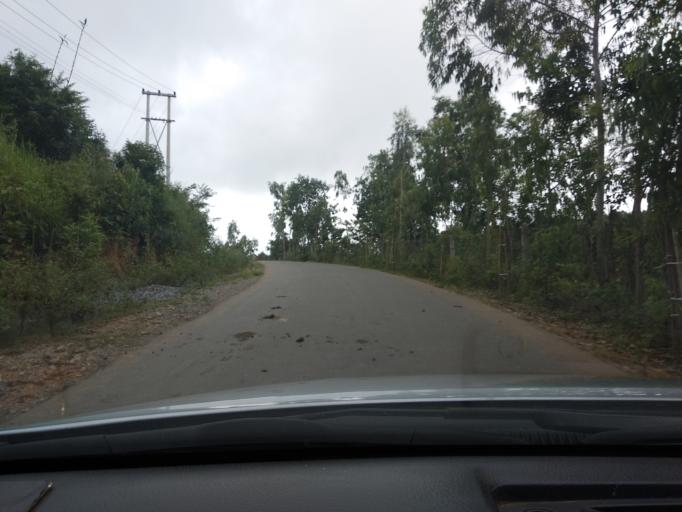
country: MM
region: Mandalay
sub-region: Pyin Oo Lwin District
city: Pyin Oo Lwin
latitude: 21.9139
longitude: 96.3829
